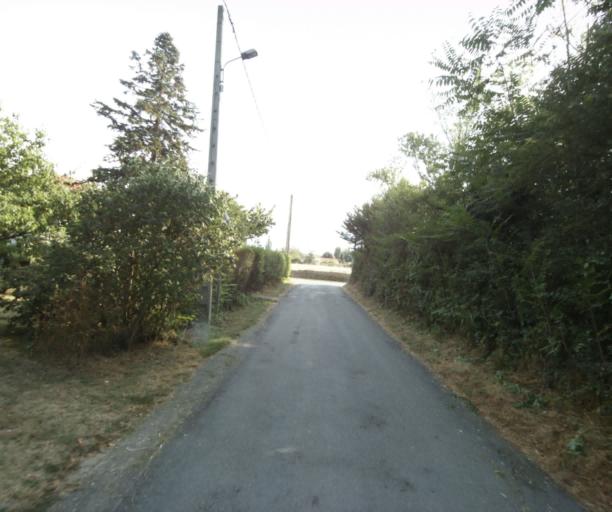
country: FR
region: Midi-Pyrenees
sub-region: Departement de la Haute-Garonne
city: Revel
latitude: 43.4710
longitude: 1.9971
